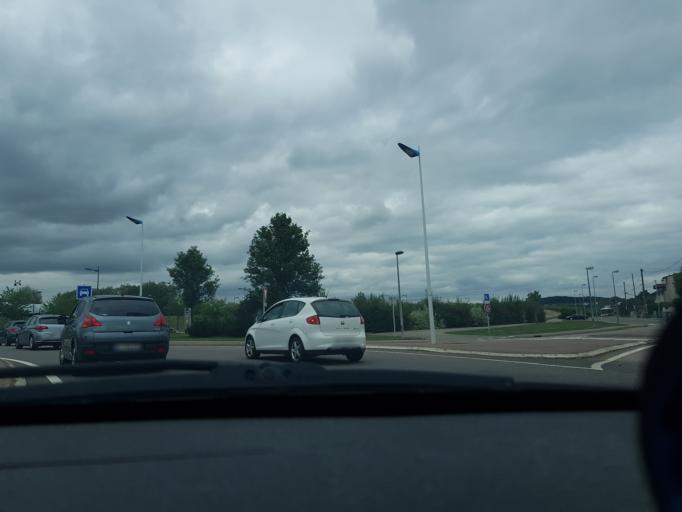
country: FR
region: Lorraine
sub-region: Departement de Meurthe-et-Moselle
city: Tomblaine
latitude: 48.6837
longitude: 6.2221
